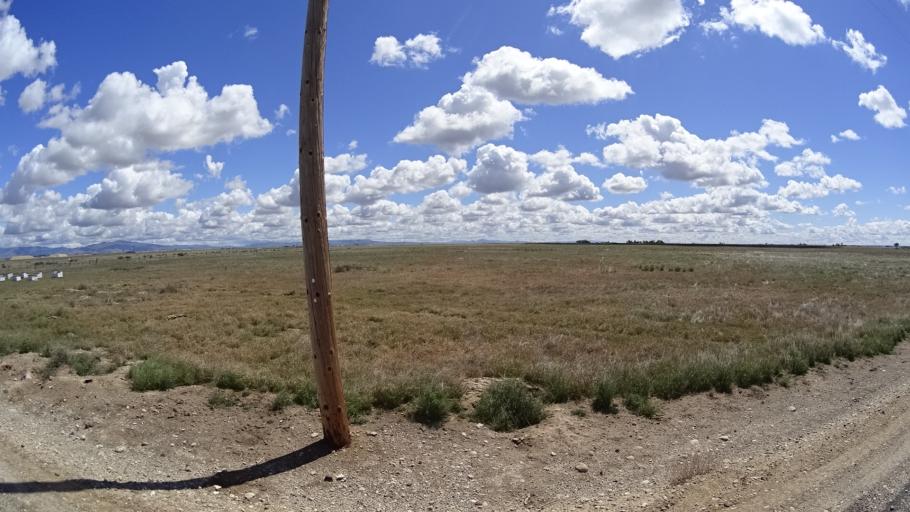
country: US
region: Idaho
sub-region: Ada County
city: Kuna
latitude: 43.4656
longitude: -116.2743
